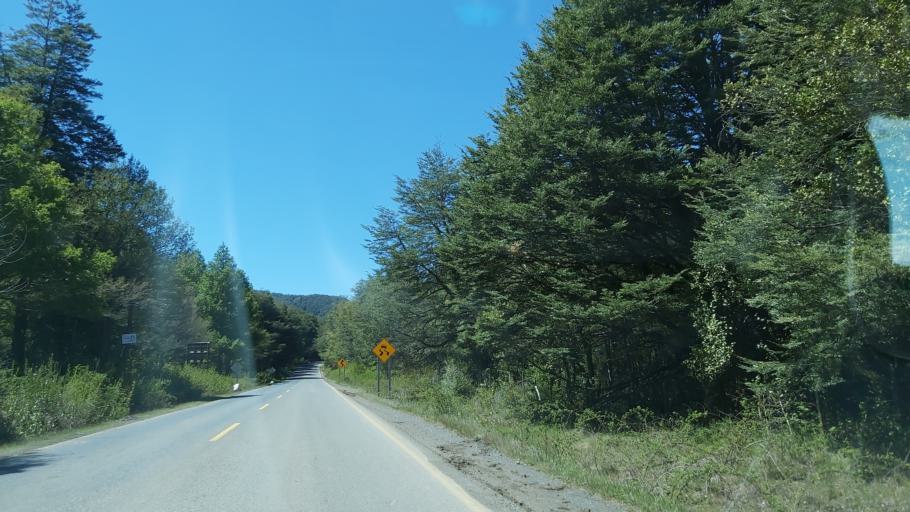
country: CL
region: Araucania
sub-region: Provincia de Cautin
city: Vilcun
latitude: -38.4699
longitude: -71.6731
